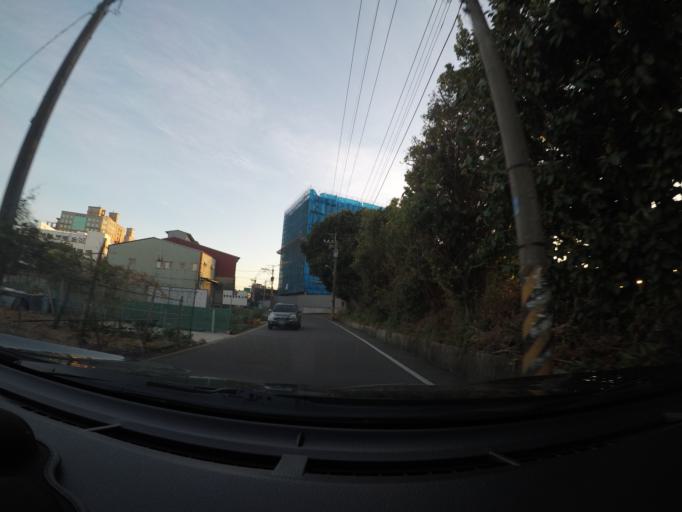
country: TW
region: Taiwan
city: Taoyuan City
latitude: 24.9946
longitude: 121.2736
